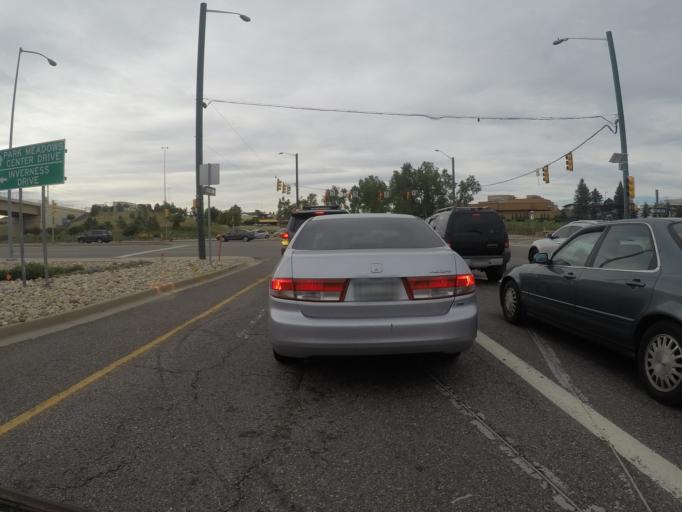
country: US
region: Colorado
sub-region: Arapahoe County
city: Centennial
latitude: 39.5665
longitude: -104.8741
